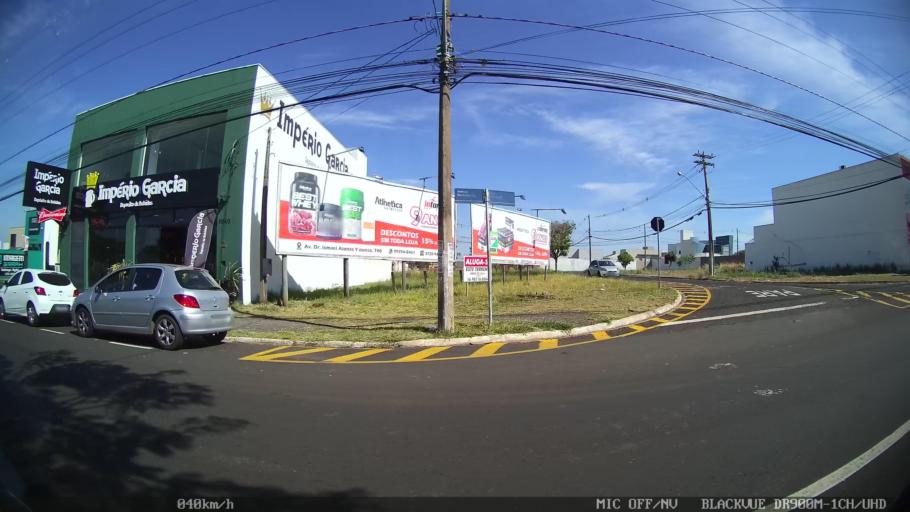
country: BR
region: Sao Paulo
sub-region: Franca
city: Franca
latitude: -20.5494
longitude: -47.4169
